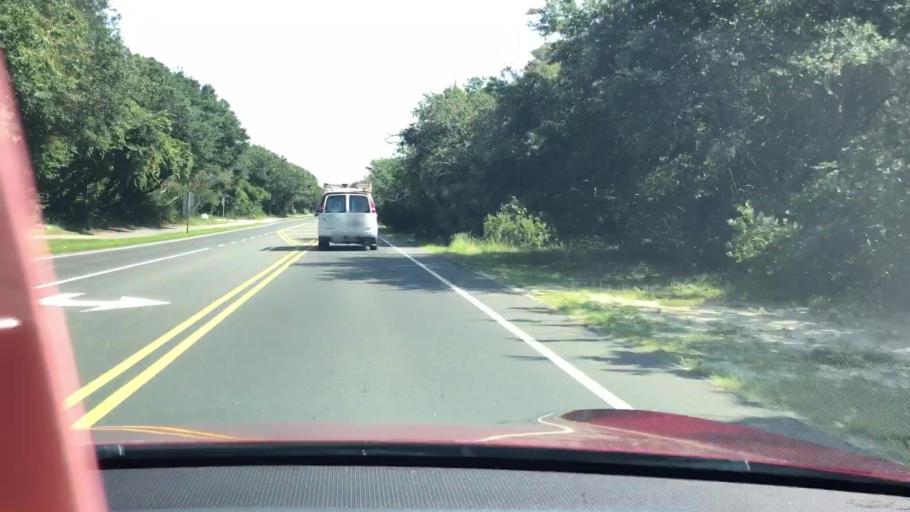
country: US
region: North Carolina
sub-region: Dare County
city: Southern Shores
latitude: 36.1440
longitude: -75.7398
